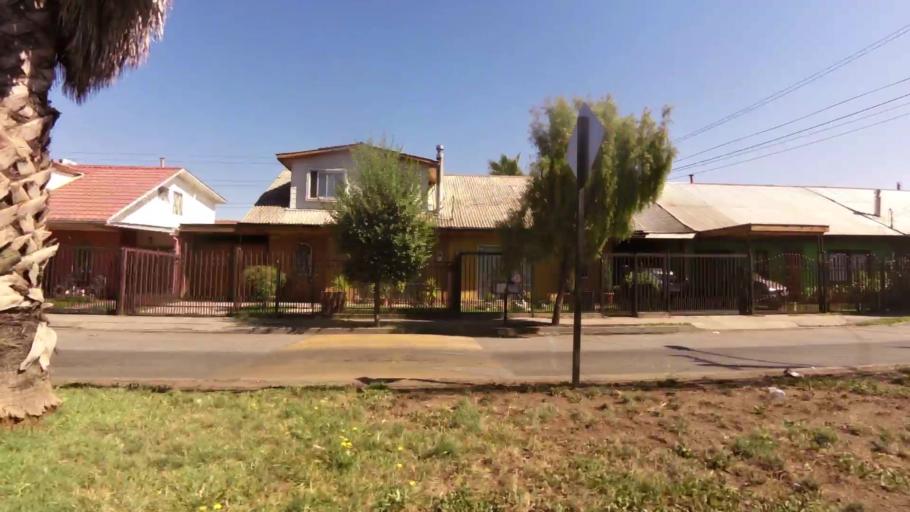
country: CL
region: Maule
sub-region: Provincia de Curico
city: Curico
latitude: -34.9740
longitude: -71.2611
